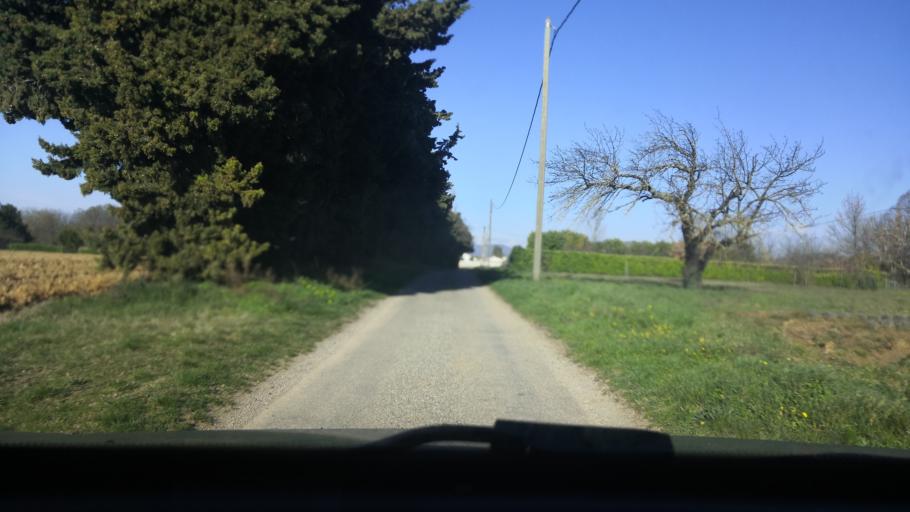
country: FR
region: Rhone-Alpes
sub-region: Departement de la Drome
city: Sauzet
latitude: 44.5764
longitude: 4.8326
